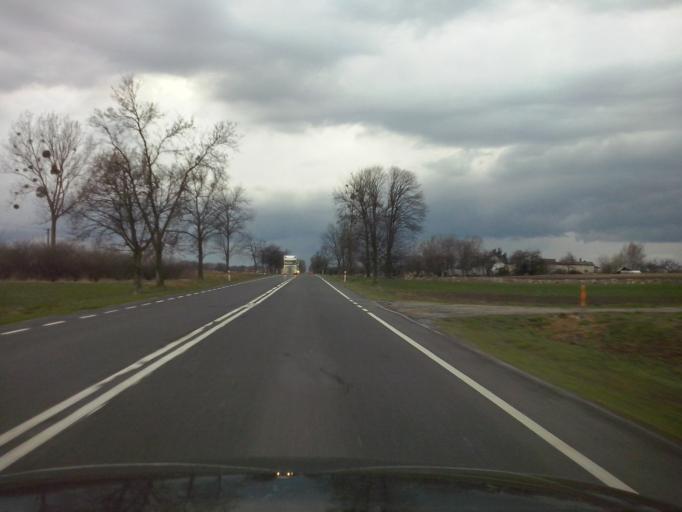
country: PL
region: Lublin Voivodeship
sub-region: Powiat chelmski
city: Rejowiec Fabryczny
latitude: 51.1714
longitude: 23.3032
